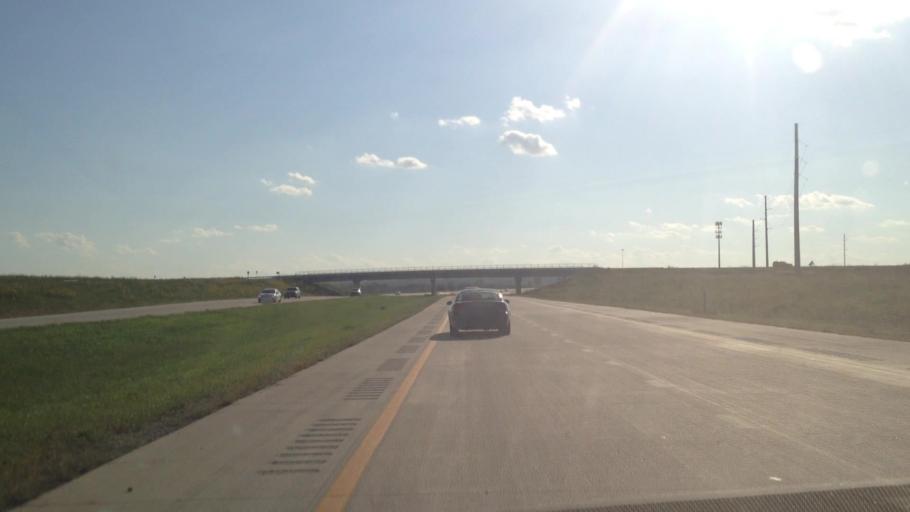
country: US
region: Kansas
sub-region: Douglas County
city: Lawrence
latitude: 38.9250
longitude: -95.2487
